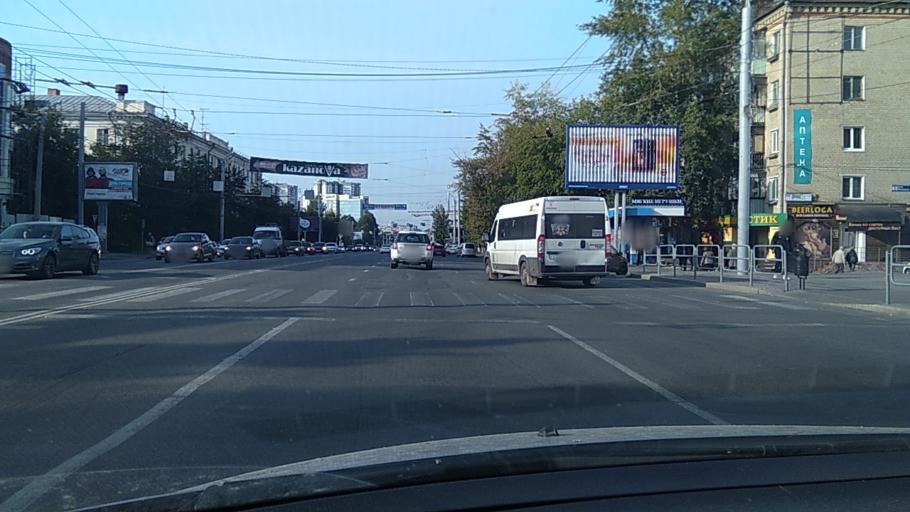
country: RU
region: Chelyabinsk
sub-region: Gorod Chelyabinsk
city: Chelyabinsk
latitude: 55.1602
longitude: 61.3812
